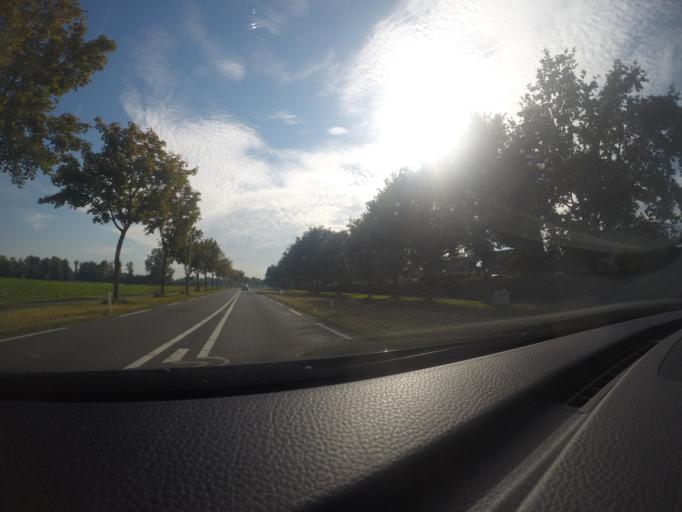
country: NL
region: Gelderland
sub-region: Gemeente Doetinchem
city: Doetinchem
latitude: 51.9619
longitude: 6.2196
